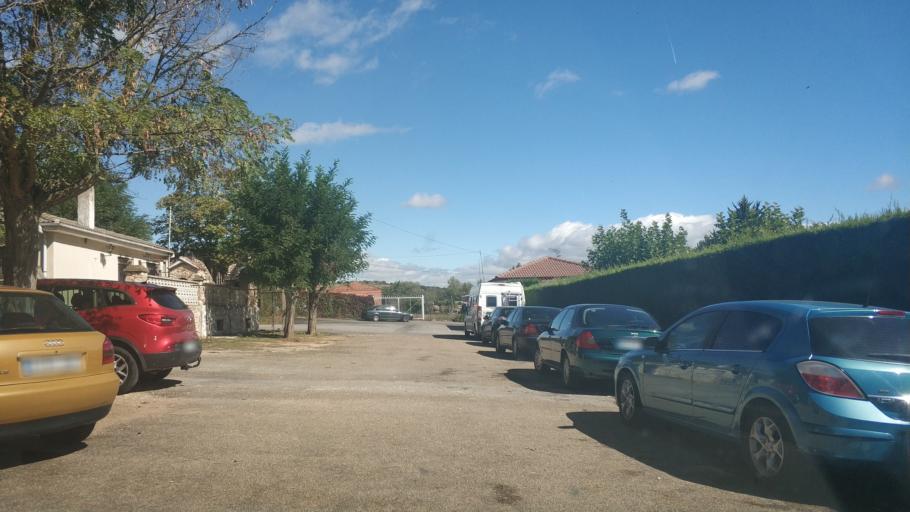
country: ES
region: Castille and Leon
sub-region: Provincia de Burgos
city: Santa Ines
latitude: 42.0313
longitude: -3.6461
